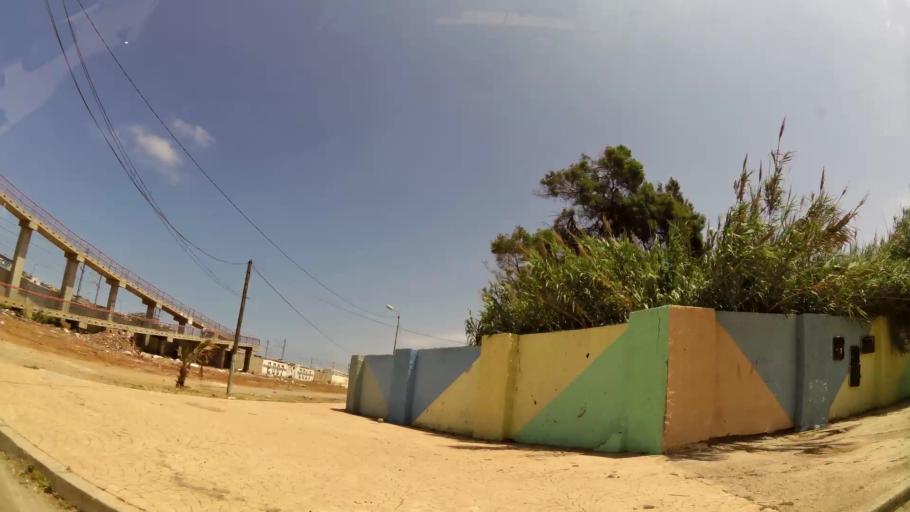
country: MA
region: Rabat-Sale-Zemmour-Zaer
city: Sale
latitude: 34.0722
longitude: -6.7853
